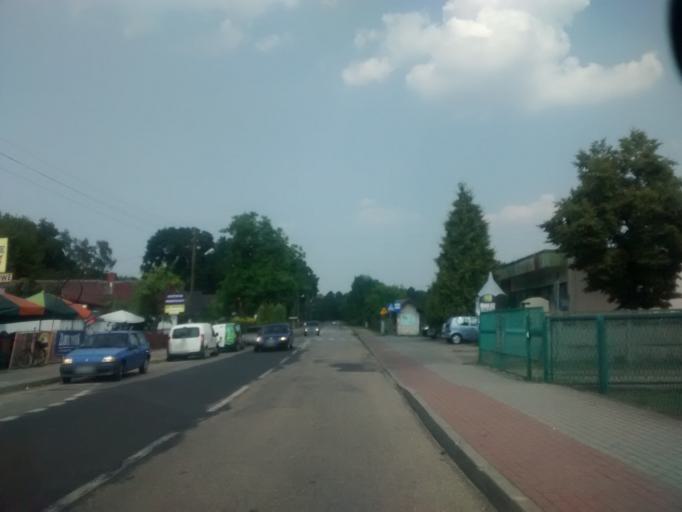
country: PL
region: Silesian Voivodeship
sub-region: Powiat czestochowski
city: Potok Zloty
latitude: 50.7086
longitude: 19.4325
